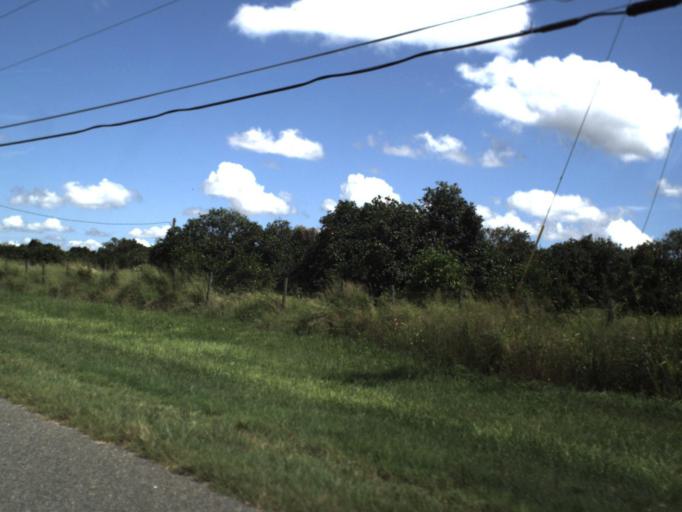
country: US
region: Florida
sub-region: Polk County
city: Lake Wales
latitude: 27.9458
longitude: -81.5951
